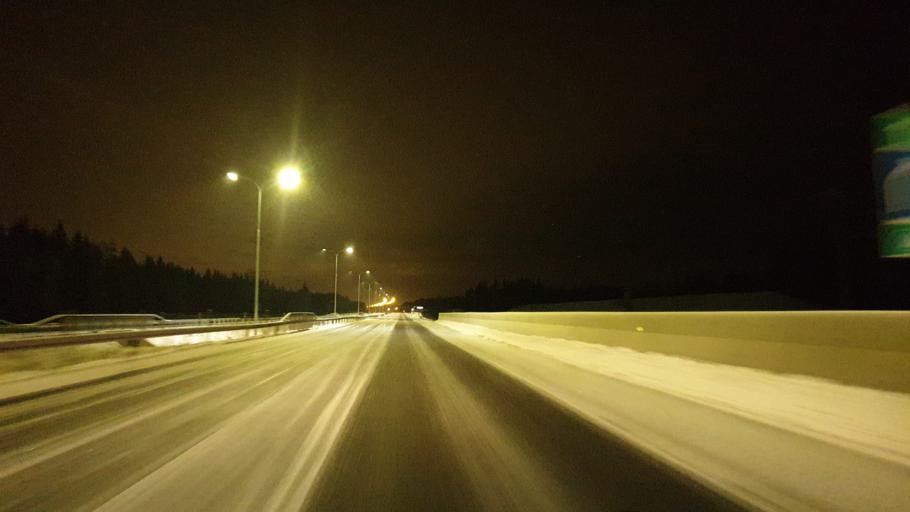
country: FI
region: Northern Ostrobothnia
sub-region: Oulu
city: Haukipudas
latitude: 65.1213
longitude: 25.4302
